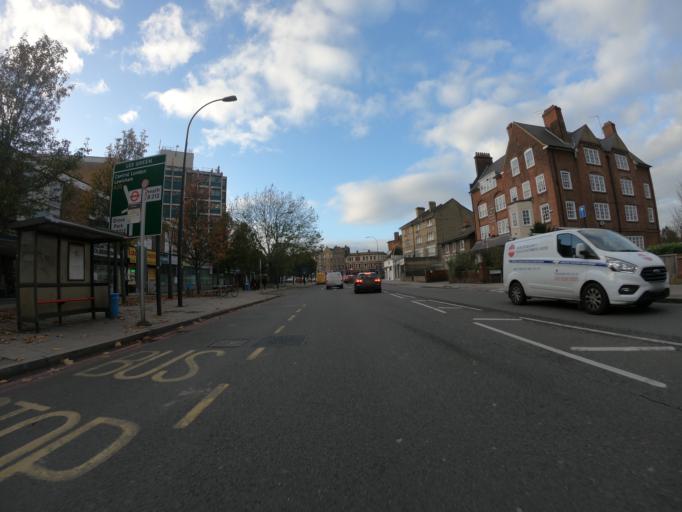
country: GB
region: England
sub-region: Greater London
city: Blackheath
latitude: 51.4561
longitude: 0.0128
